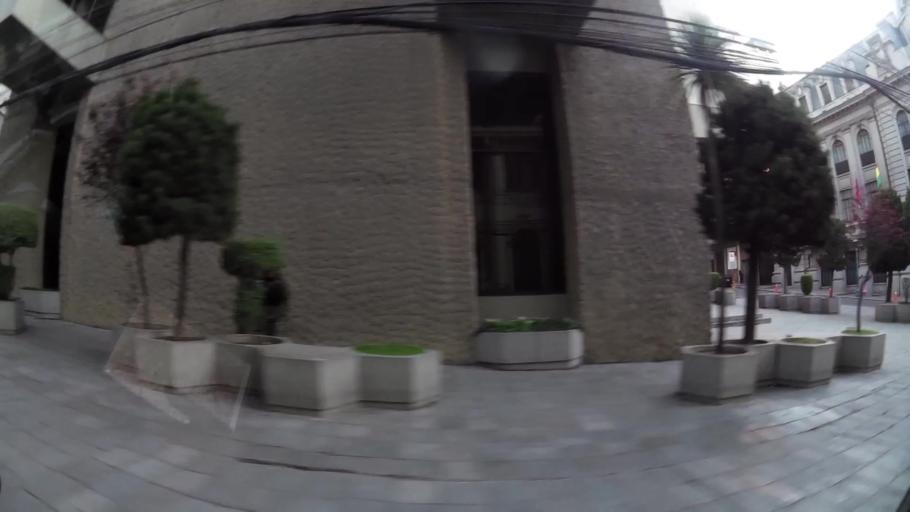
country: BO
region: La Paz
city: La Paz
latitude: -16.4974
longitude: -68.1345
